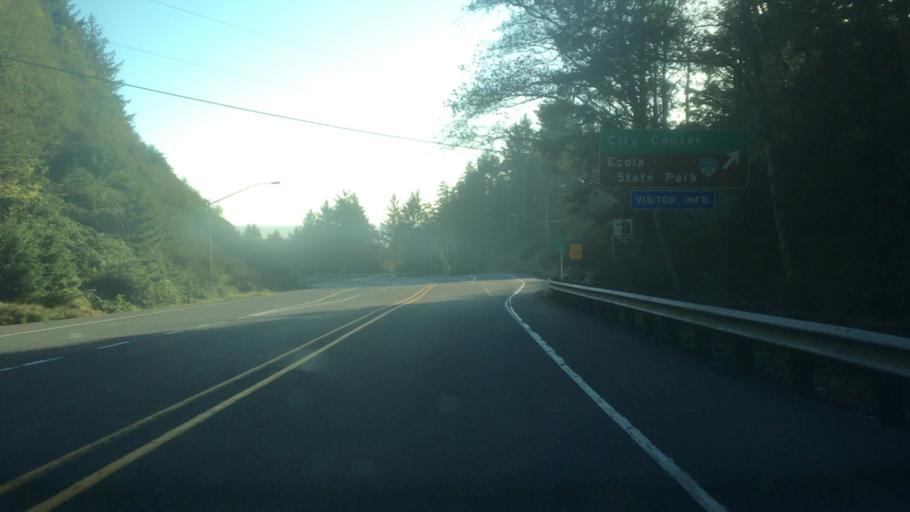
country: US
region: Oregon
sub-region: Clatsop County
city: Cannon Beach
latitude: 45.9079
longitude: -123.9523
